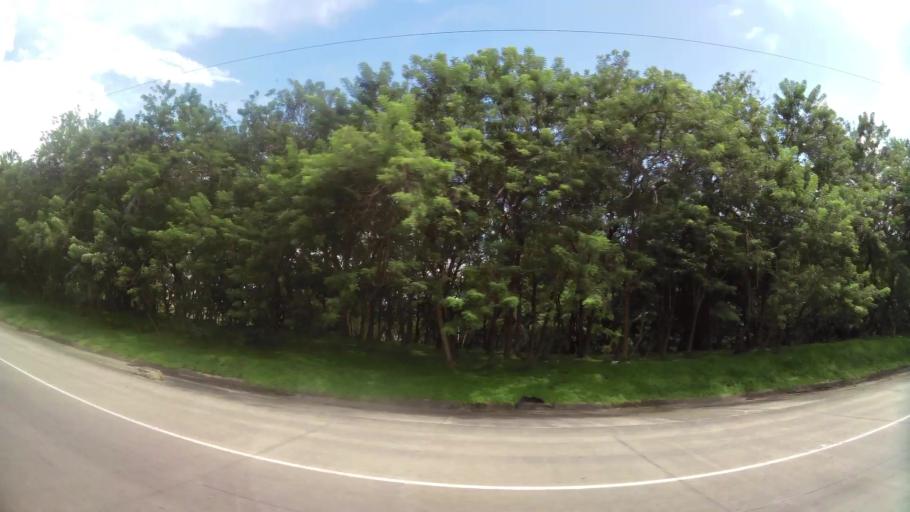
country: PA
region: Panama
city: Panama
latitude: 9.0406
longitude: -79.5318
